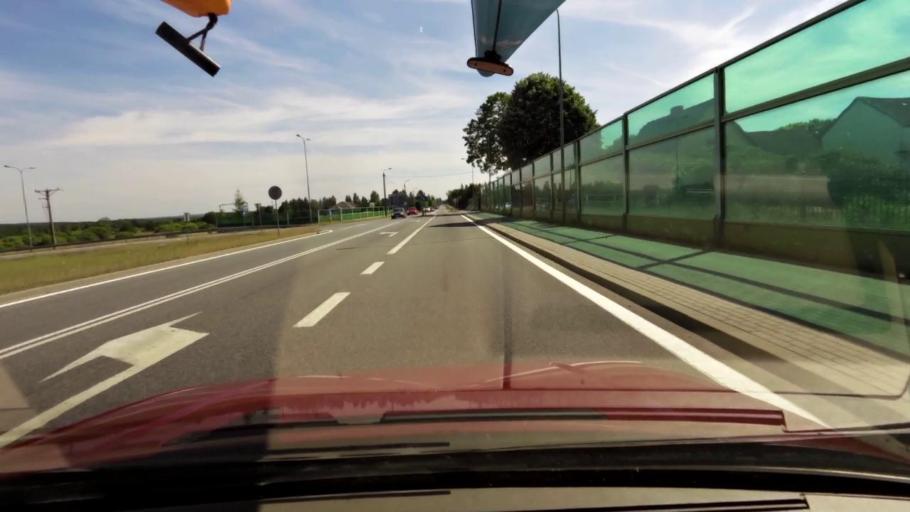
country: PL
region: Pomeranian Voivodeship
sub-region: Powiat slupski
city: Kobylnica
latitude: 54.4243
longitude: 17.0071
